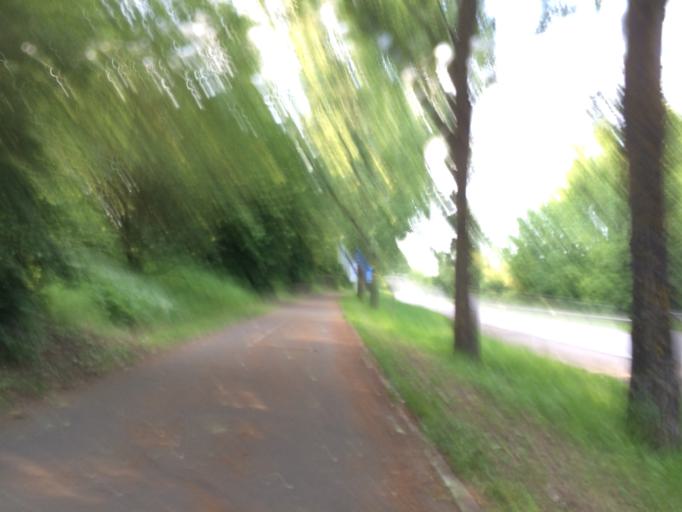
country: FR
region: Ile-de-France
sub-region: Departement de l'Essonne
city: Lisses
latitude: 48.6072
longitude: 2.4256
